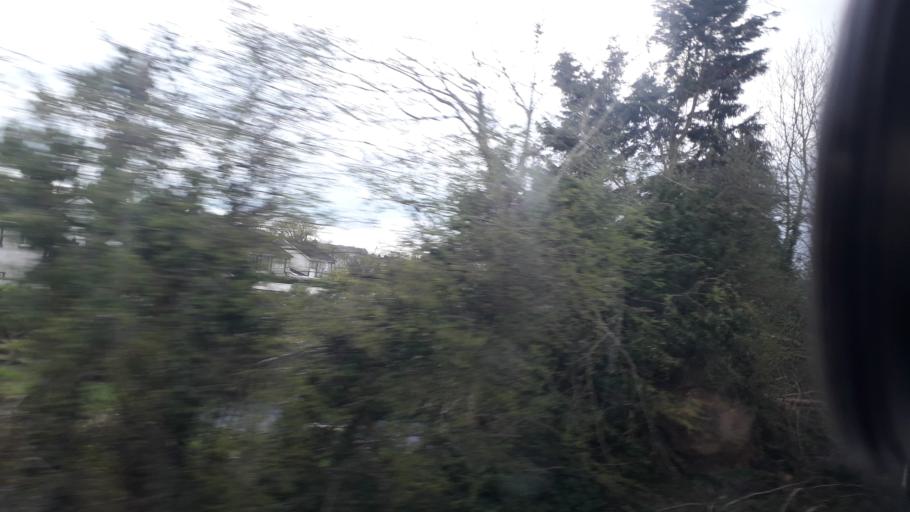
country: IE
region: Leinster
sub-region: An Longfort
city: Longford
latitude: 53.7264
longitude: -7.7799
